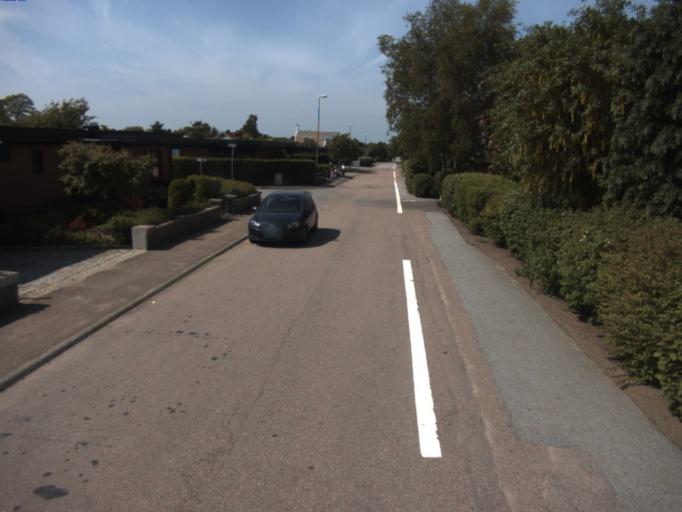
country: SE
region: Skane
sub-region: Helsingborg
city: Helsingborg
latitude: 56.0908
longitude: 12.6566
